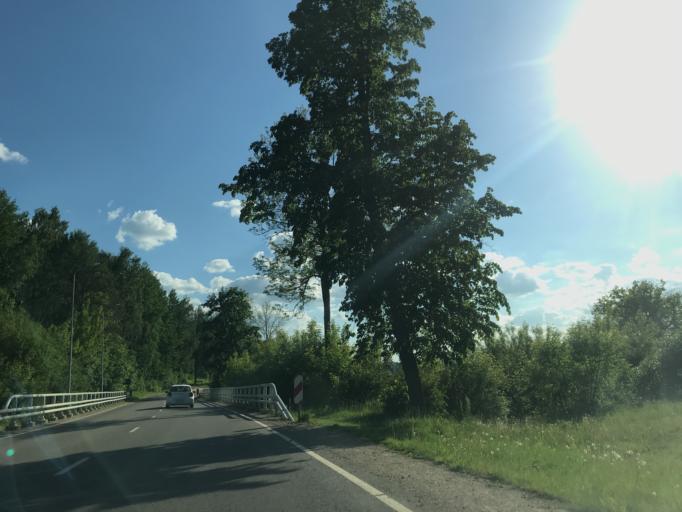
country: LV
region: Jaunjelgava
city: Jaunjelgava
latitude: 56.6094
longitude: 25.0522
